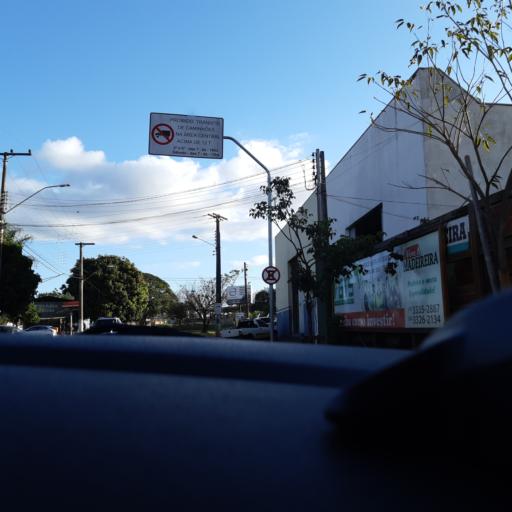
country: BR
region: Sao Paulo
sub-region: Ourinhos
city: Ourinhos
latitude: -22.9844
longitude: -49.8577
